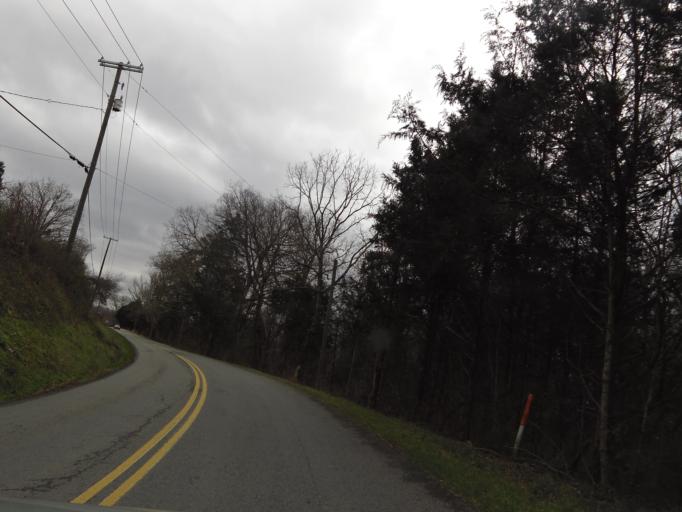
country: US
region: Tennessee
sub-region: Grainger County
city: Blaine
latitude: 36.1400
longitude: -83.6740
